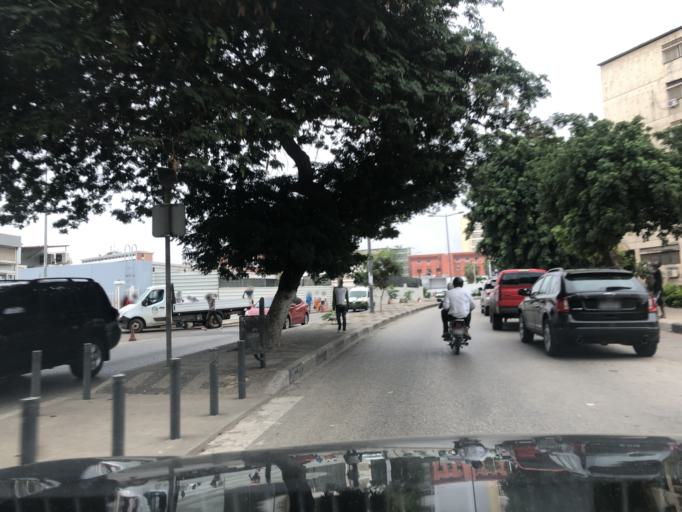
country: AO
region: Luanda
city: Luanda
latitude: -8.8265
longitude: 13.2389
